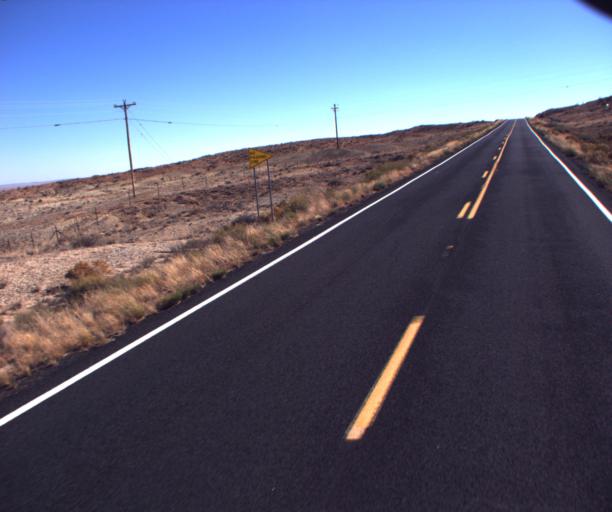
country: US
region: Arizona
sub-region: Coconino County
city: Tuba City
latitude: 35.9952
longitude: -111.0237
